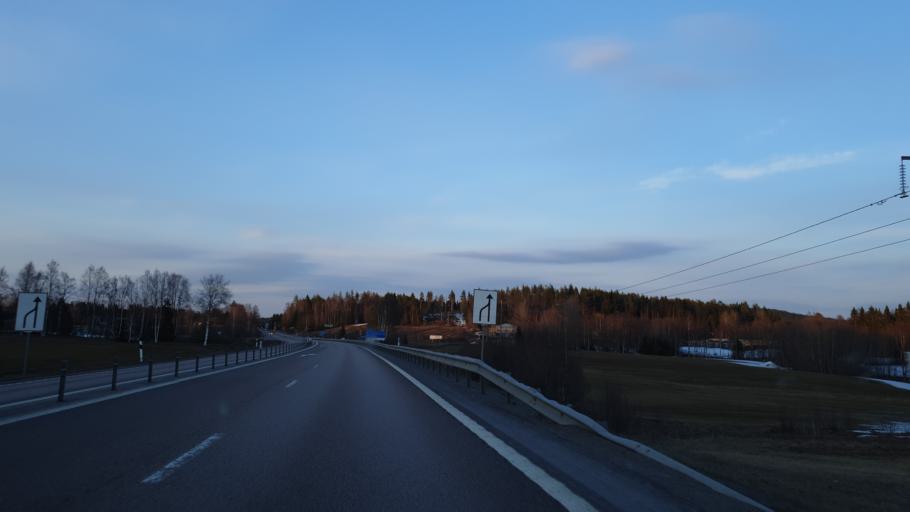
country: SE
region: Vaesternorrland
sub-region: Haernoesands Kommun
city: Haernoesand
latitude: 62.5861
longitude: 17.7825
